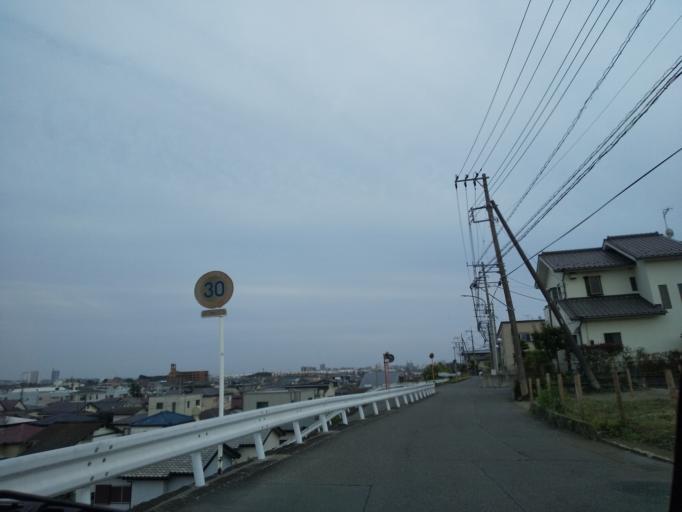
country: JP
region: Kanagawa
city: Atsugi
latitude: 35.4725
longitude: 139.3533
